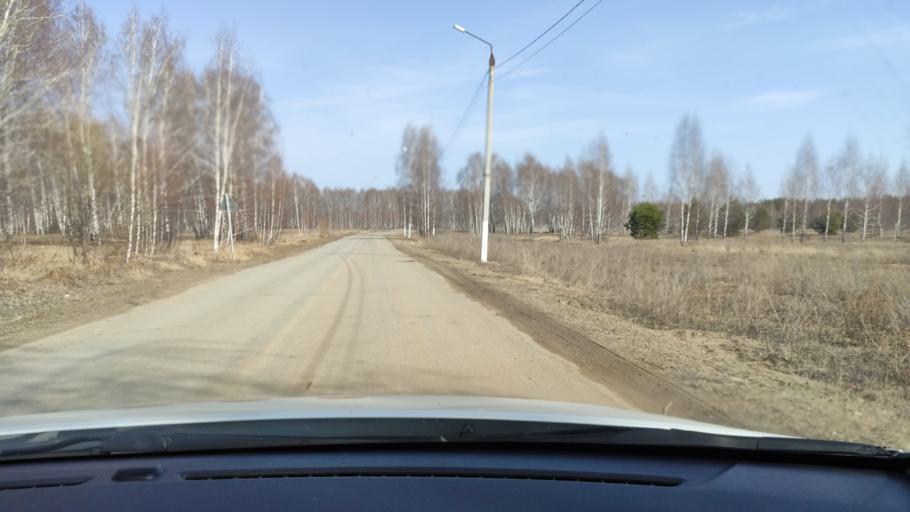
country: RU
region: Tatarstan
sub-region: Gorod Kazan'
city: Kazan
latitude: 55.6919
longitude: 49.1175
